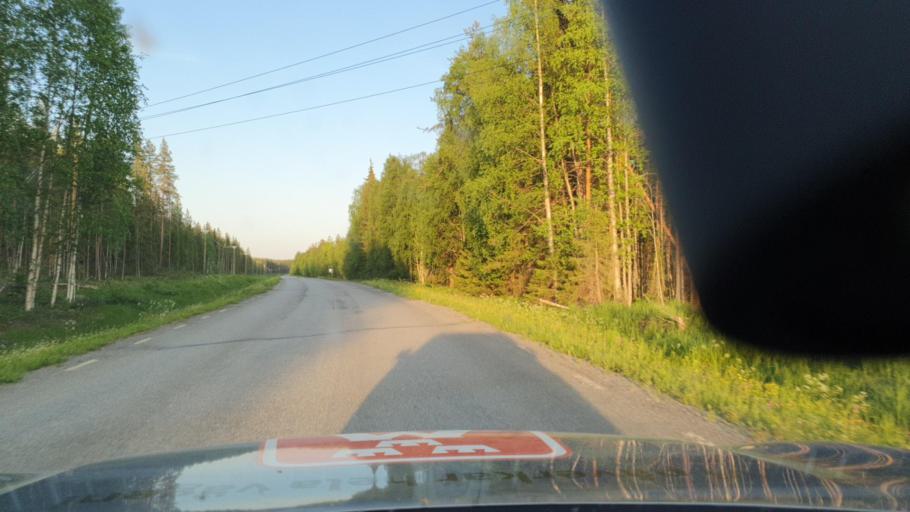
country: SE
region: Norrbotten
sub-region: Bodens Kommun
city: Boden
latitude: 66.0189
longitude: 21.8181
